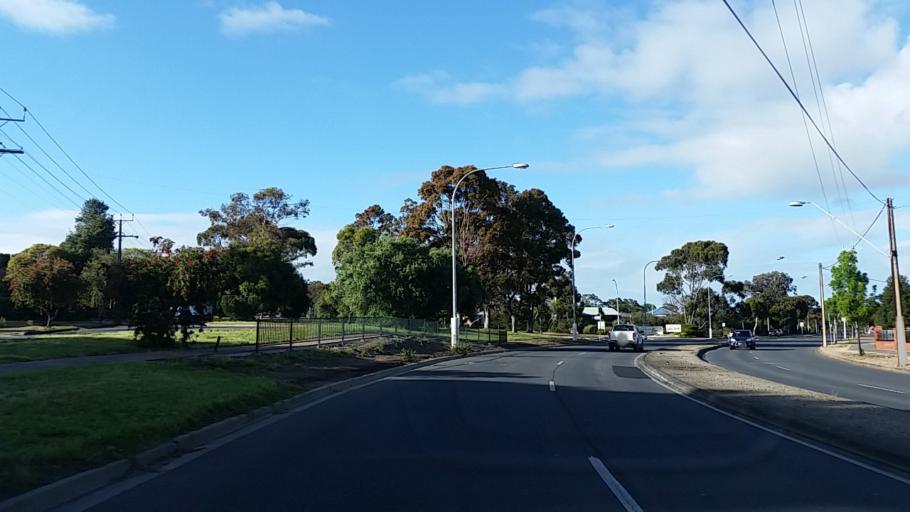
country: AU
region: South Australia
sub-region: Mitcham
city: Clapham
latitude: -34.9991
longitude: 138.5932
